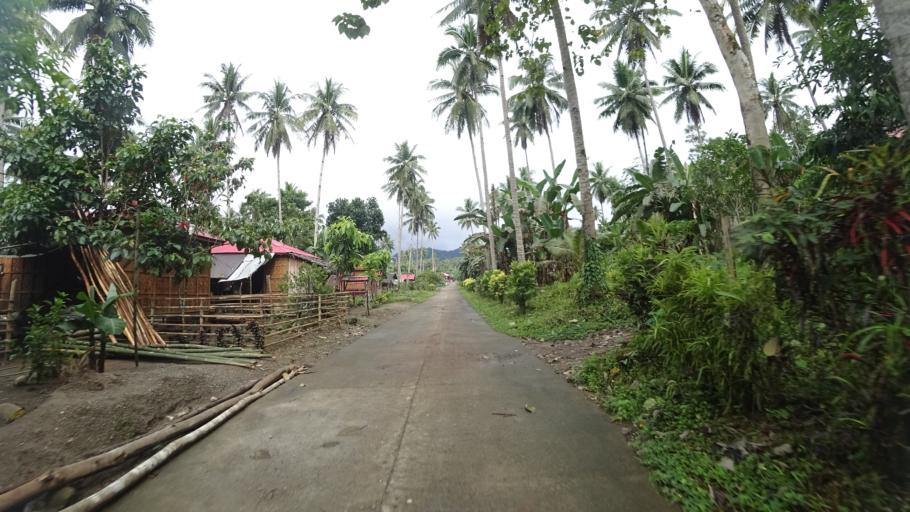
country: PH
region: Eastern Visayas
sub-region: Province of Leyte
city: Bugho
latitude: 10.8277
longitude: 124.8945
